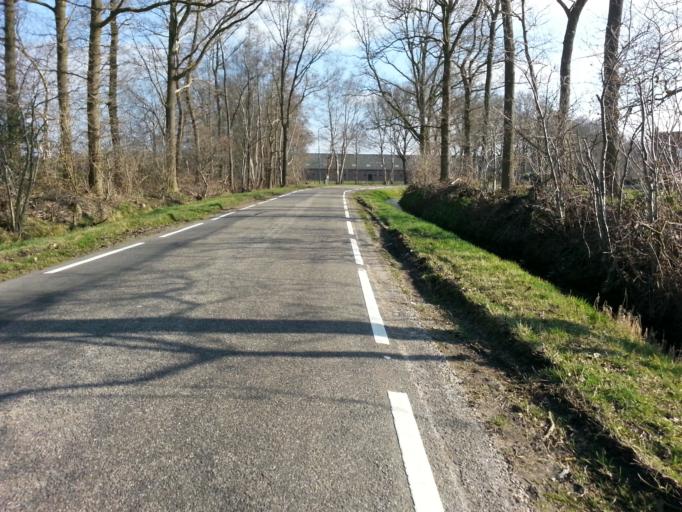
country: NL
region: Utrecht
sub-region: Gemeente Leusden
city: Leusden
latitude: 52.0966
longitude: 5.4744
